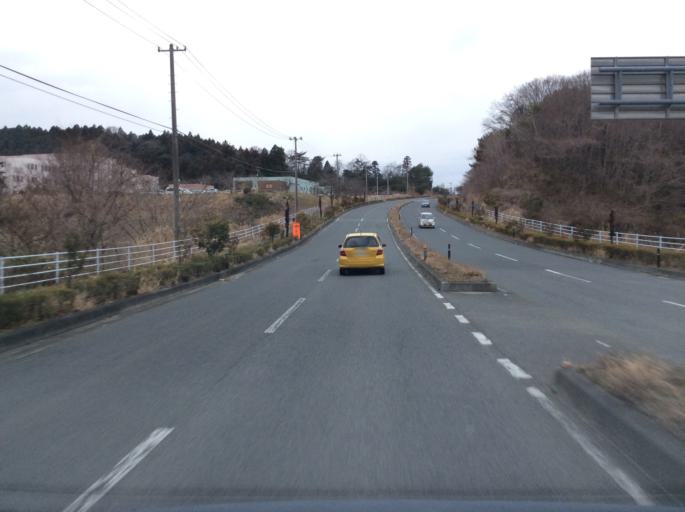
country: JP
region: Fukushima
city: Iwaki
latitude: 36.9711
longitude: 140.9121
